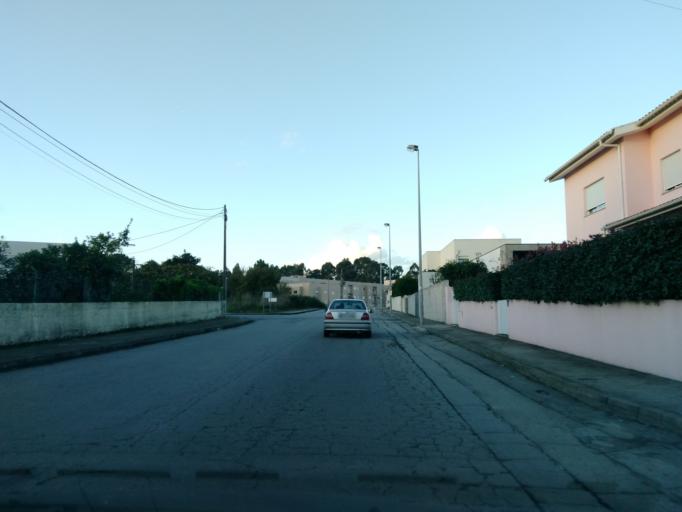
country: PT
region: Braga
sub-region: Braga
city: Braga
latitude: 41.5290
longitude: -8.4547
